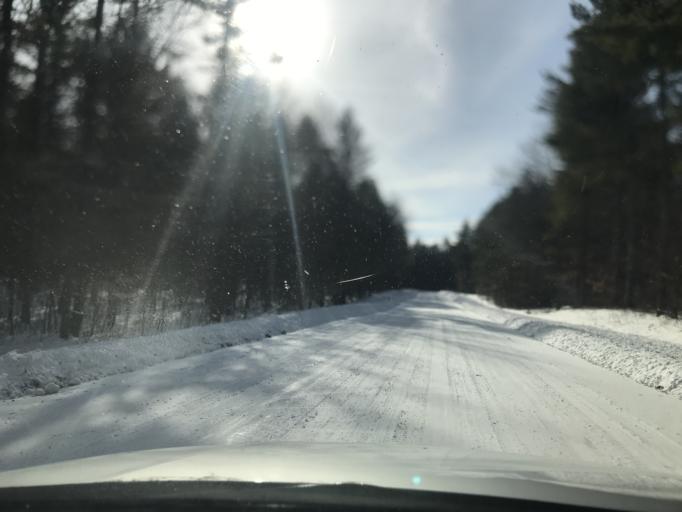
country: US
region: Wisconsin
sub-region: Oconto County
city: Gillett
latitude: 45.1384
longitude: -88.2490
